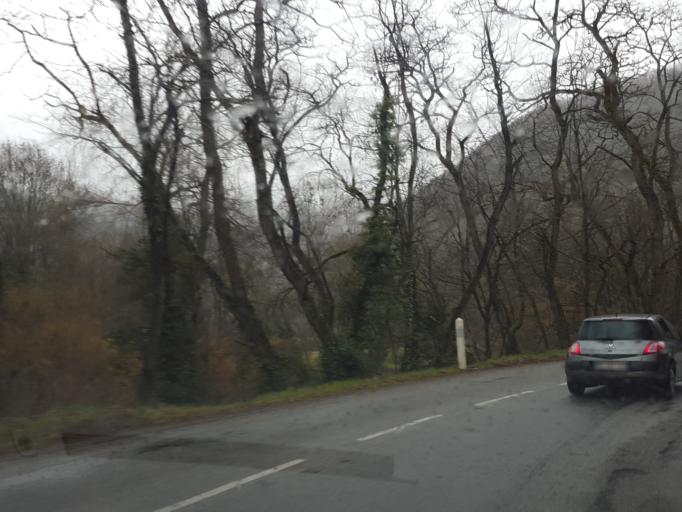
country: FR
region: Midi-Pyrenees
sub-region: Departement de l'Ariege
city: Saint-Girons
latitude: 42.9050
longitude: 1.2449
